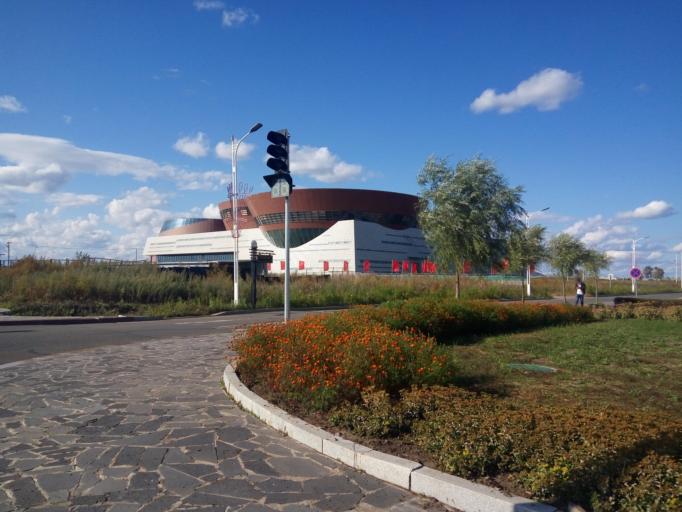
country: CN
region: Heilongjiang Sheng
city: Erjing
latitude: 48.6297
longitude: 126.1151
